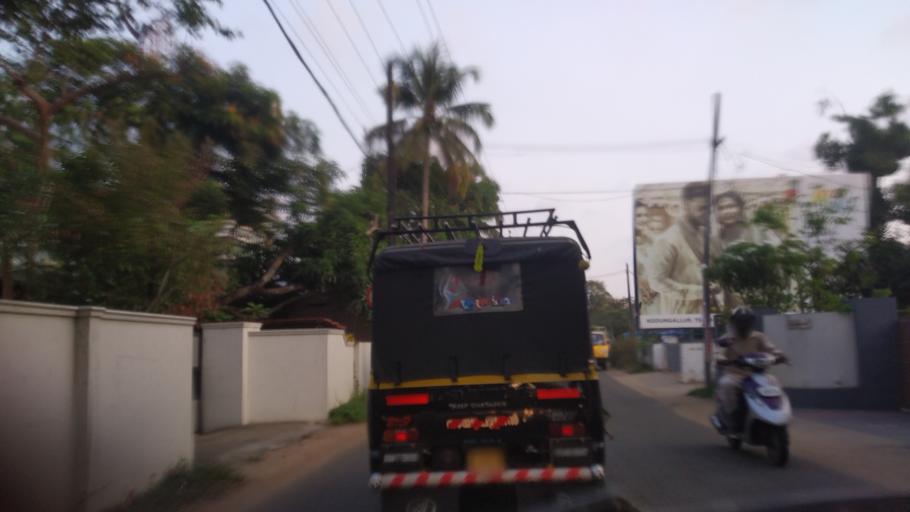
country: IN
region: Kerala
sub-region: Thrissur District
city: Kodungallur
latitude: 10.2370
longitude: 76.1530
